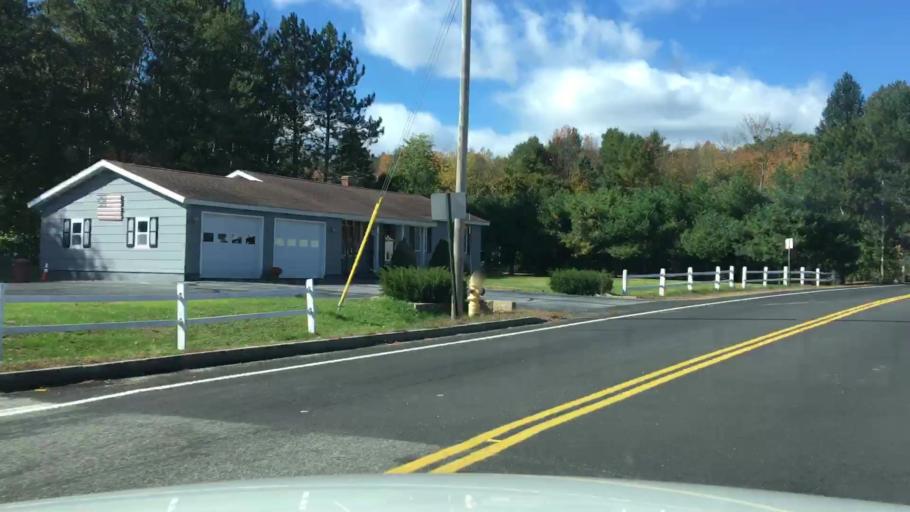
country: US
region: Maine
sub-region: York County
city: Biddeford
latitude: 43.4558
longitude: -70.4298
